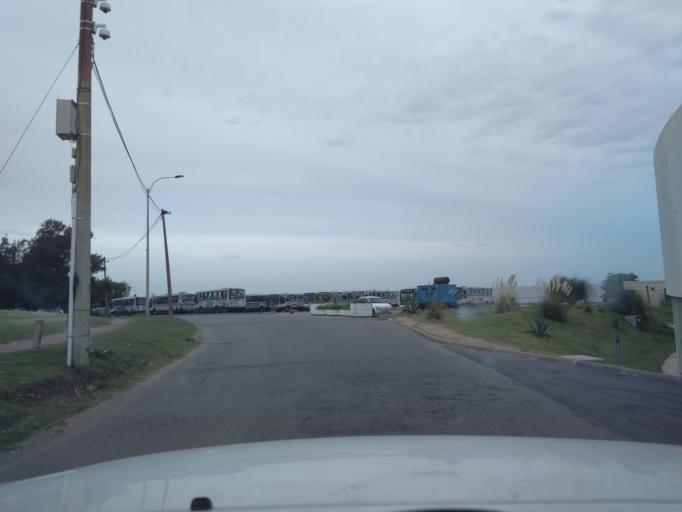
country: UY
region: Montevideo
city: Montevideo
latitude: -34.9112
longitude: -56.1385
